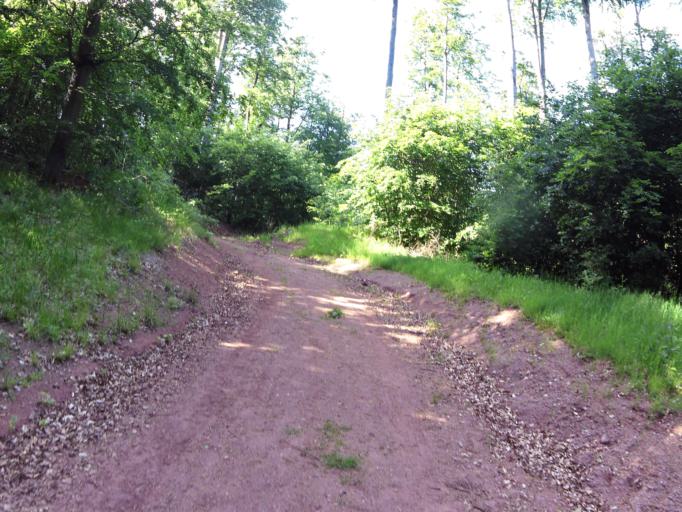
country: DE
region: Thuringia
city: Wolfsburg-Unkeroda
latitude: 50.9265
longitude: 10.3080
